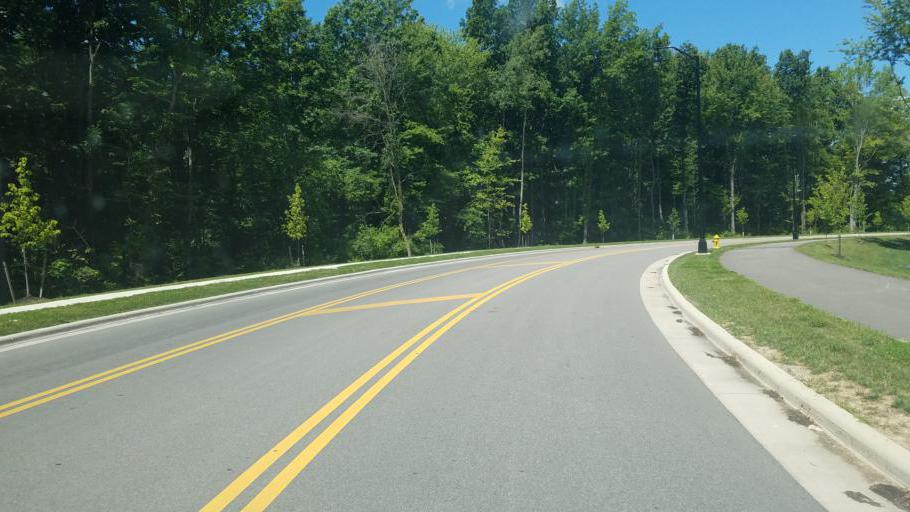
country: US
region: Ohio
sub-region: Delaware County
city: Sunbury
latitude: 40.2632
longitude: -82.9230
